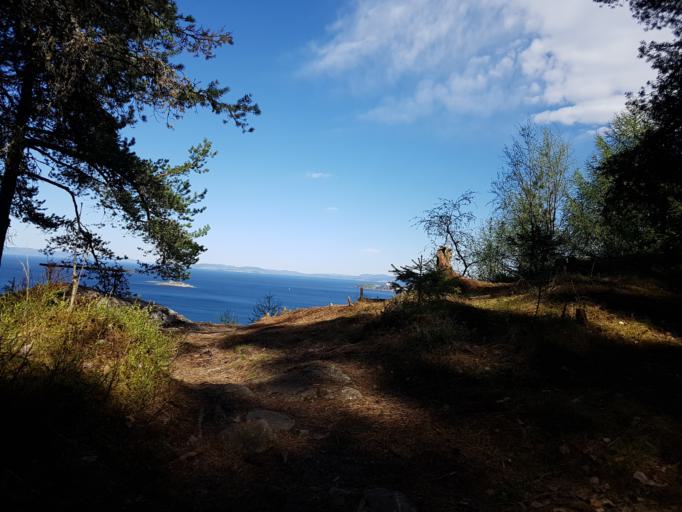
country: NO
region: Sor-Trondelag
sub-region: Trondheim
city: Trondheim
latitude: 63.4335
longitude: 10.3459
